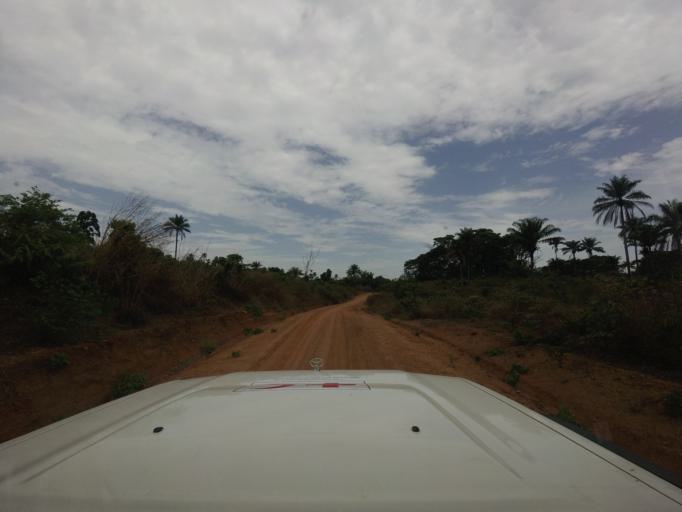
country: SL
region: Eastern Province
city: Buedu
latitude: 8.2554
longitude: -10.2308
